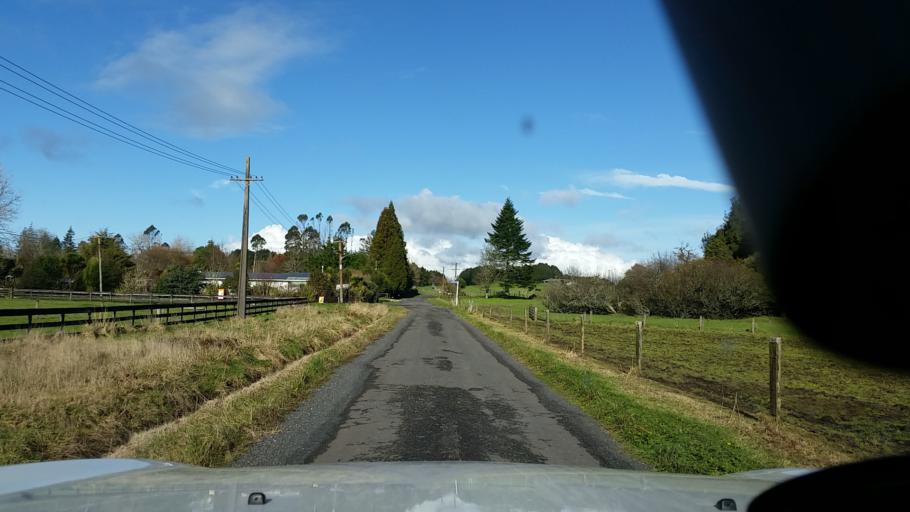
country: NZ
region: Bay of Plenty
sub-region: Rotorua District
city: Rotorua
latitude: -38.0990
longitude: 176.0743
